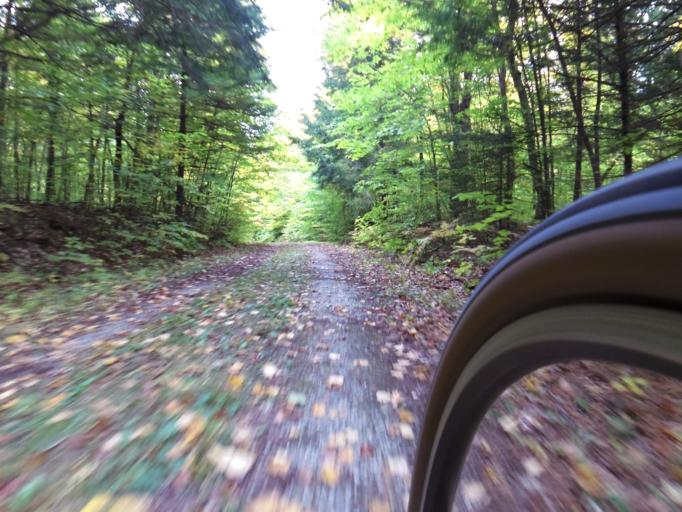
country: CA
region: Quebec
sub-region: Outaouais
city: Wakefield
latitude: 45.5972
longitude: -76.0680
